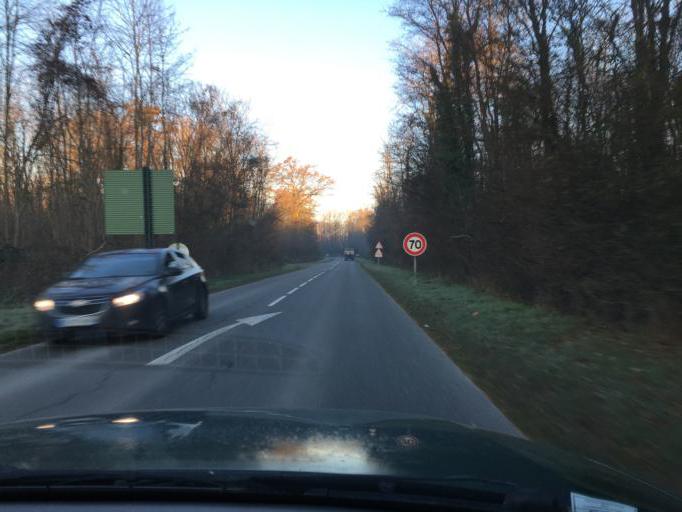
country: FR
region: Centre
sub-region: Departement du Loiret
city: Saran
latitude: 47.9663
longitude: 1.8684
